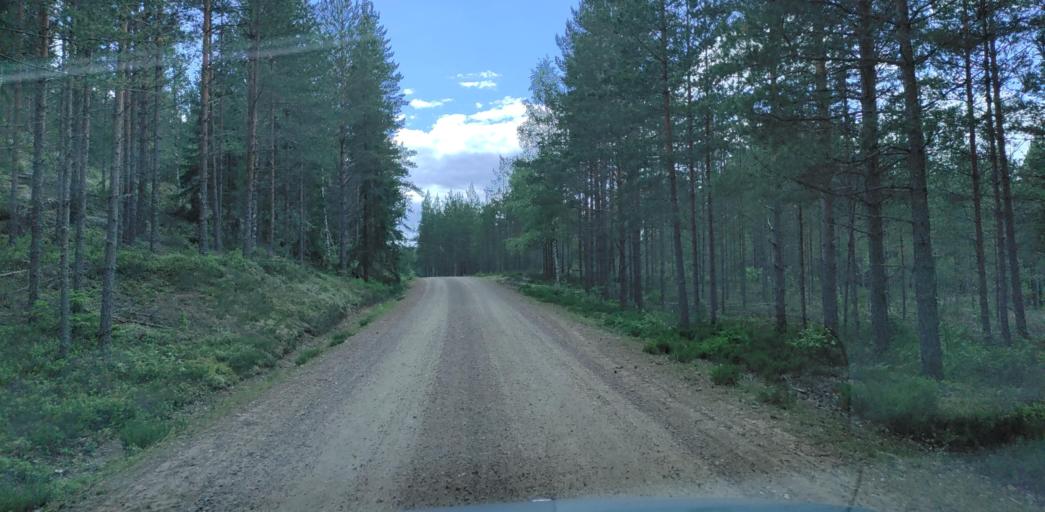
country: SE
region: Vaermland
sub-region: Hagfors Kommun
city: Ekshaerad
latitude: 60.0830
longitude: 13.2979
